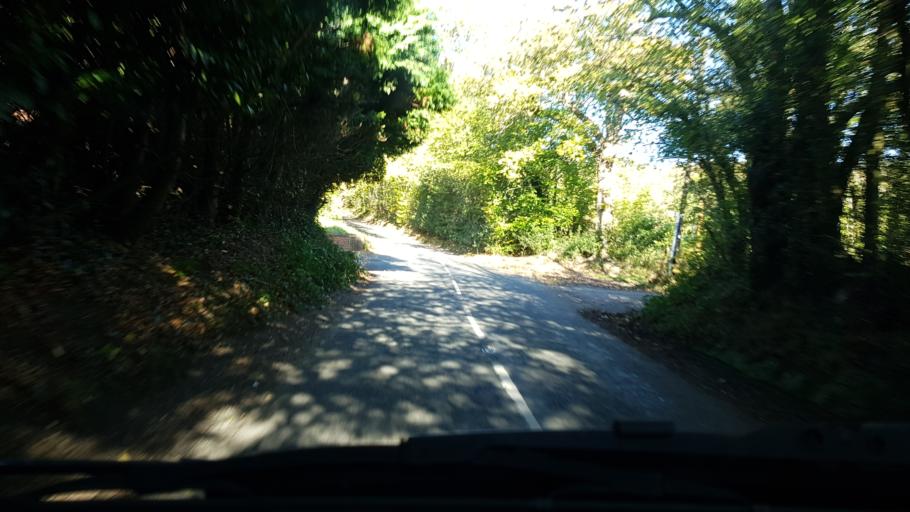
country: GB
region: England
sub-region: Surrey
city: Ockley
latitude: 51.1772
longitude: -0.4081
